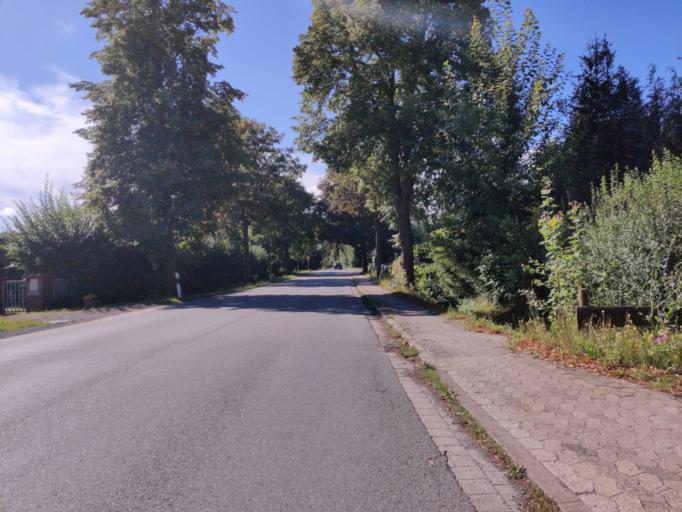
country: DE
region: Lower Saxony
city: Holle
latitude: 52.1067
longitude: 10.1646
